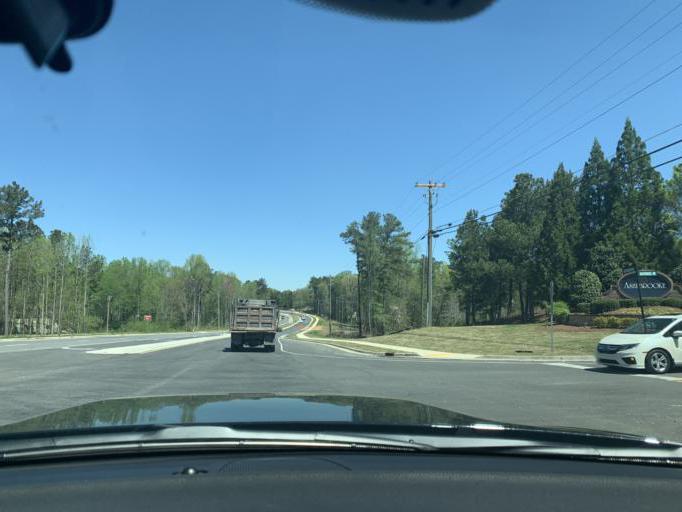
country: US
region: Georgia
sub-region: Forsyth County
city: Cumming
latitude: 34.2084
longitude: -84.1979
